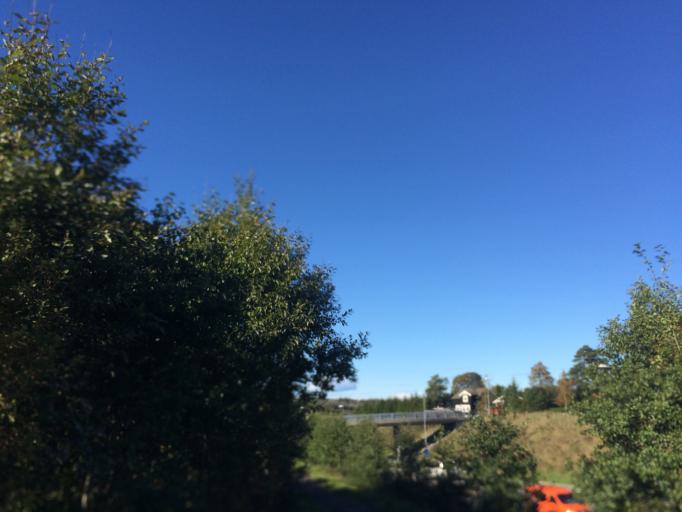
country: NO
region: Akershus
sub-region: Ski
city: Ski
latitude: 59.7232
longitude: 10.7913
